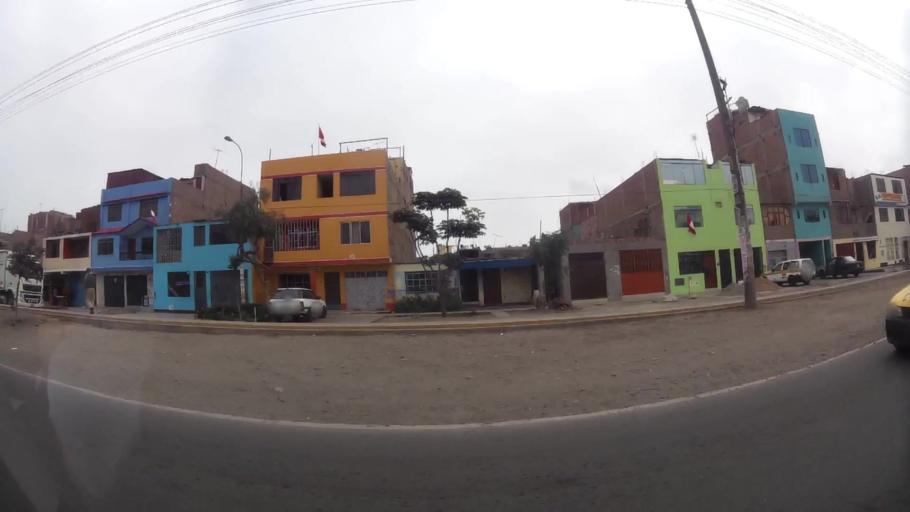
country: PE
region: Lima
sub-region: Lima
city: Independencia
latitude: -12.0164
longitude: -77.0781
